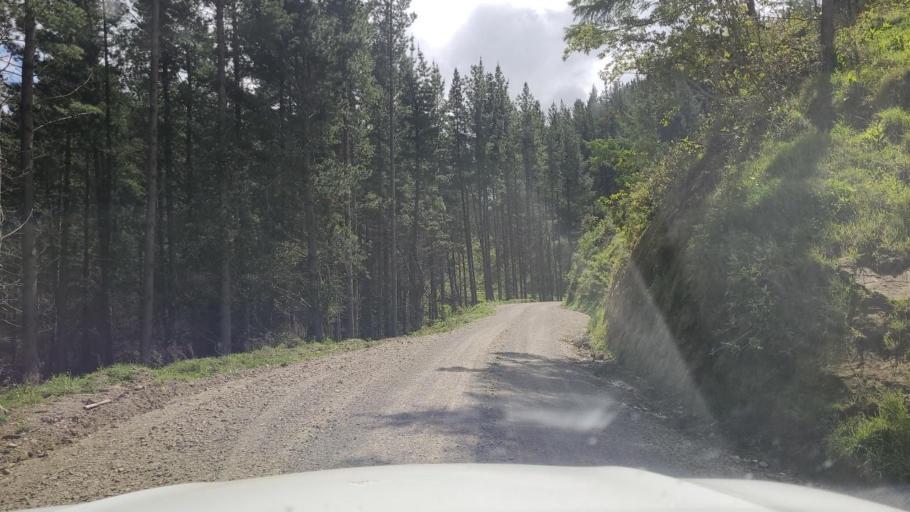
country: NZ
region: Hawke's Bay
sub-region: Napier City
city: Taradale
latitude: -39.2682
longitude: 176.6551
